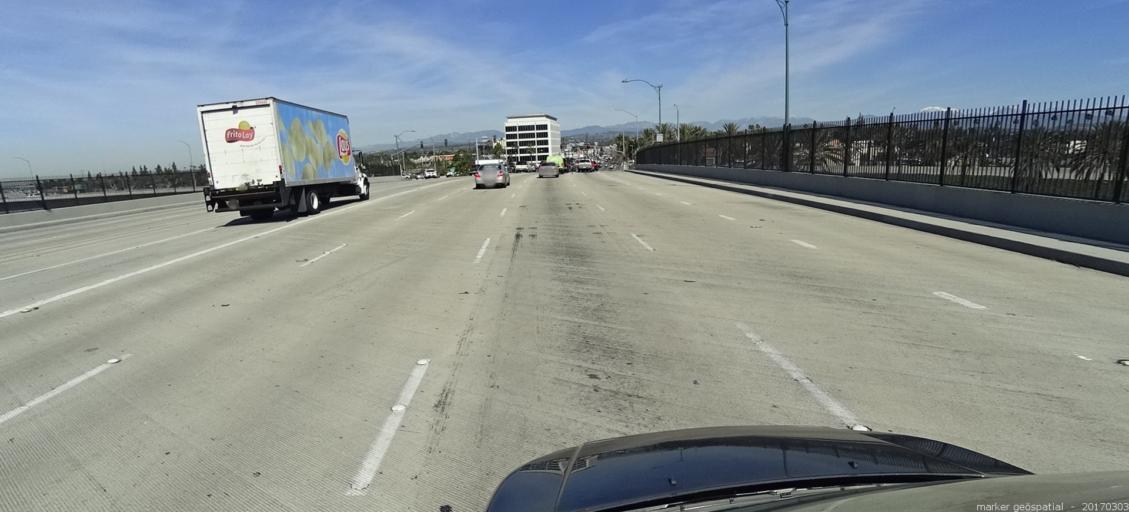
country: US
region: California
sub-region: Orange County
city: Anaheim
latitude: 33.8354
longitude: -117.9414
